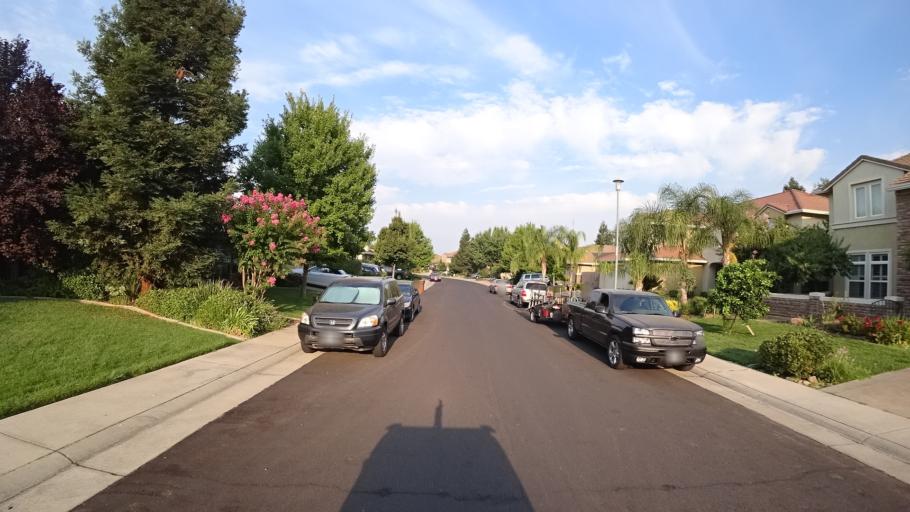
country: US
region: California
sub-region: Sacramento County
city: Laguna
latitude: 38.3824
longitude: -121.4195
